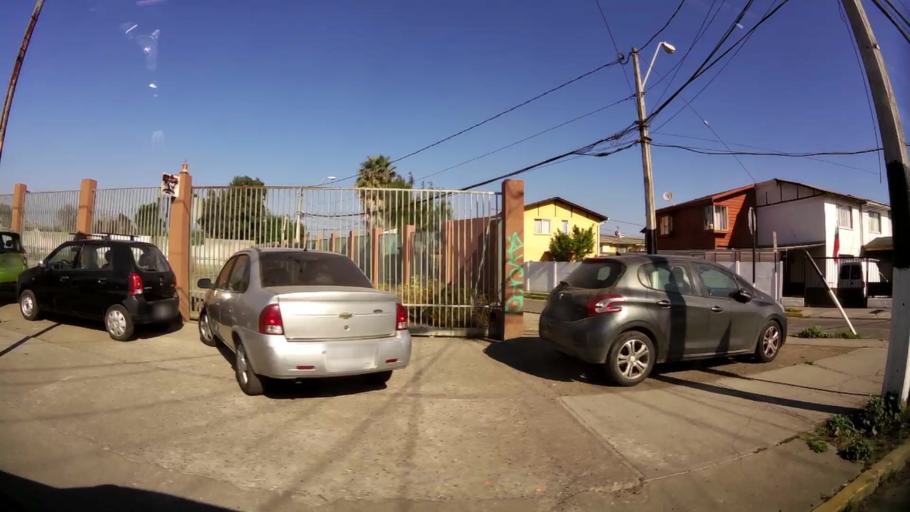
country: CL
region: Santiago Metropolitan
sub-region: Provincia de Santiago
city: Lo Prado
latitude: -33.4867
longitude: -70.7660
